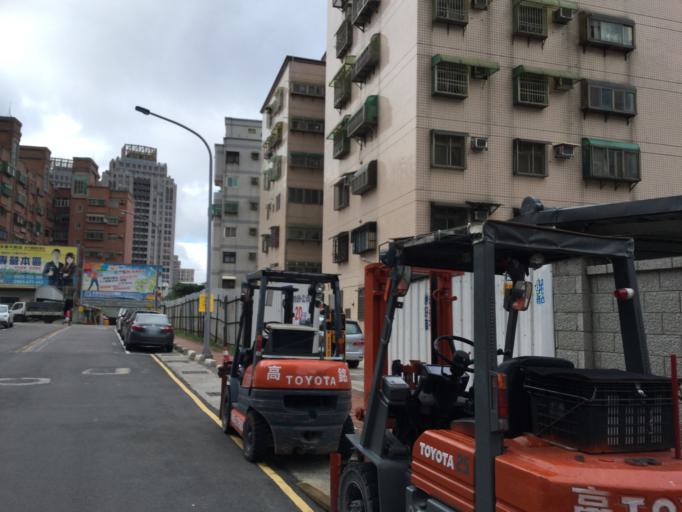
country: TW
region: Taiwan
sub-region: Hsinchu
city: Hsinchu
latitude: 24.7861
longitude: 121.0172
